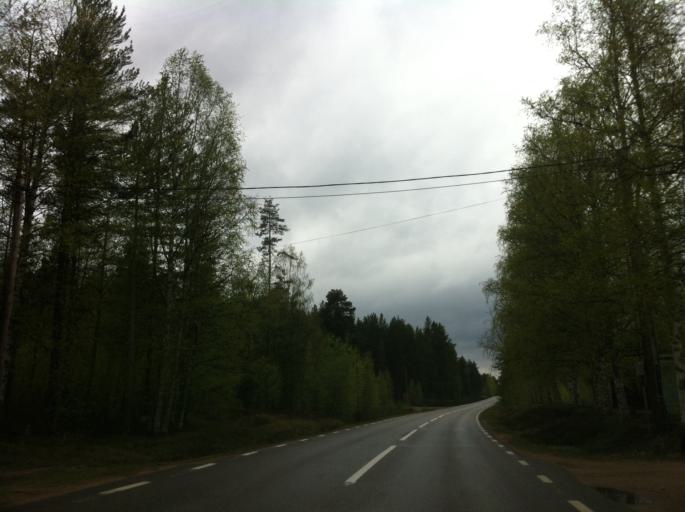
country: SE
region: Jaemtland
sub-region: Harjedalens Kommun
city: Sveg
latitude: 62.0246
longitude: 14.4446
